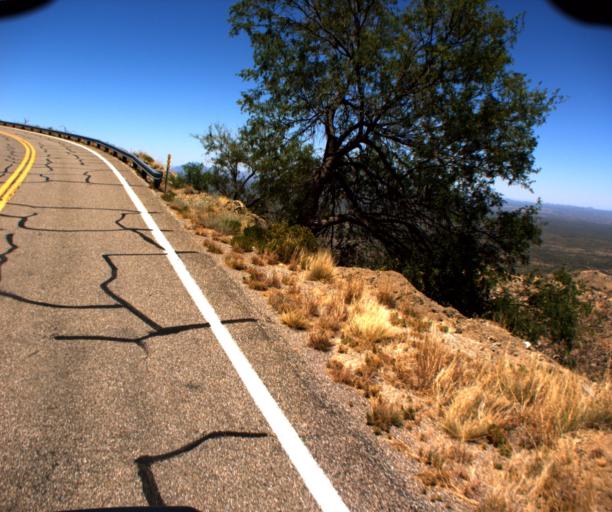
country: US
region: Arizona
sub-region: Pima County
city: Sells
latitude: 31.9750
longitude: -111.6058
